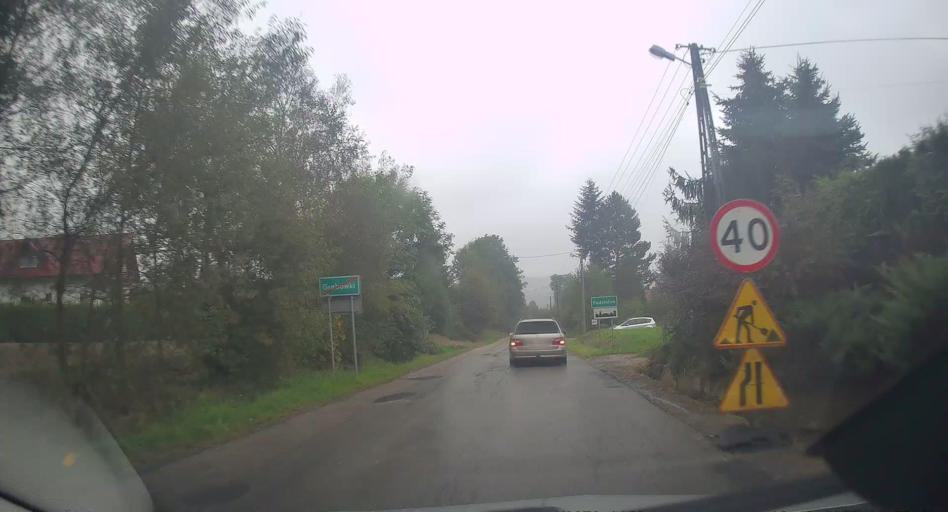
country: PL
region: Lesser Poland Voivodeship
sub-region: Powiat krakowski
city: Ochojno
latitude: 49.9732
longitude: 20.0002
